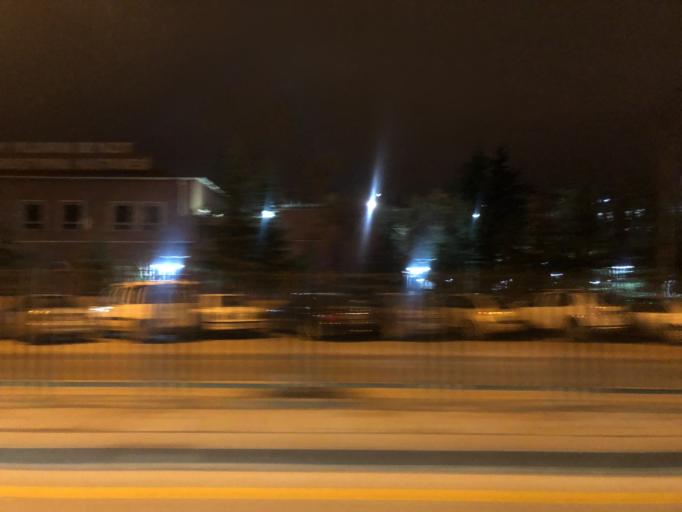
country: TR
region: Ankara
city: Ankara
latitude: 39.9560
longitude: 32.8622
